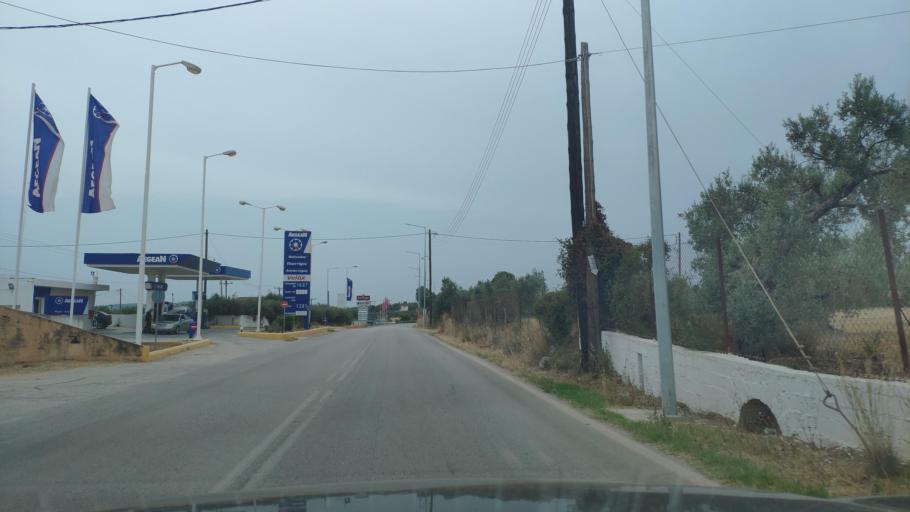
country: GR
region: Peloponnese
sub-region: Nomos Argolidos
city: Porto Cheli
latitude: 37.3444
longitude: 23.1576
